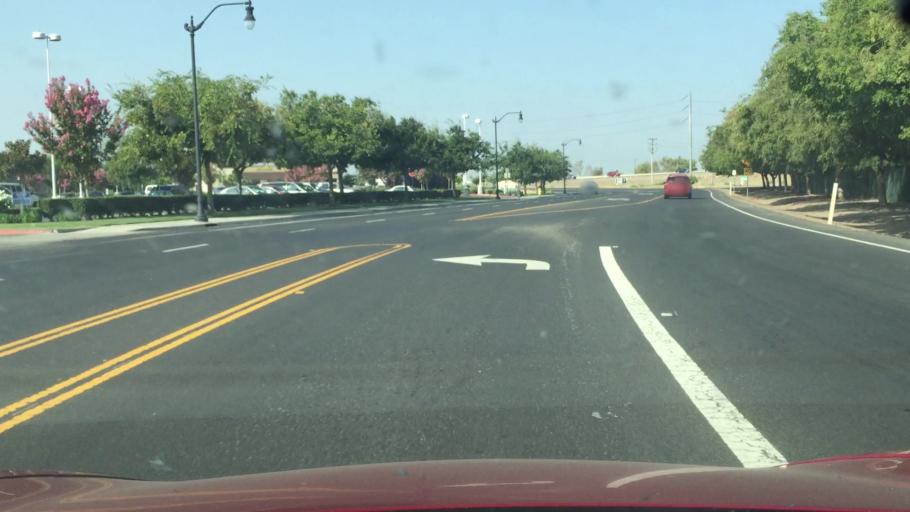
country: US
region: California
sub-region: San Joaquin County
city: Lathrop
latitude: 37.8247
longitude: -121.2880
